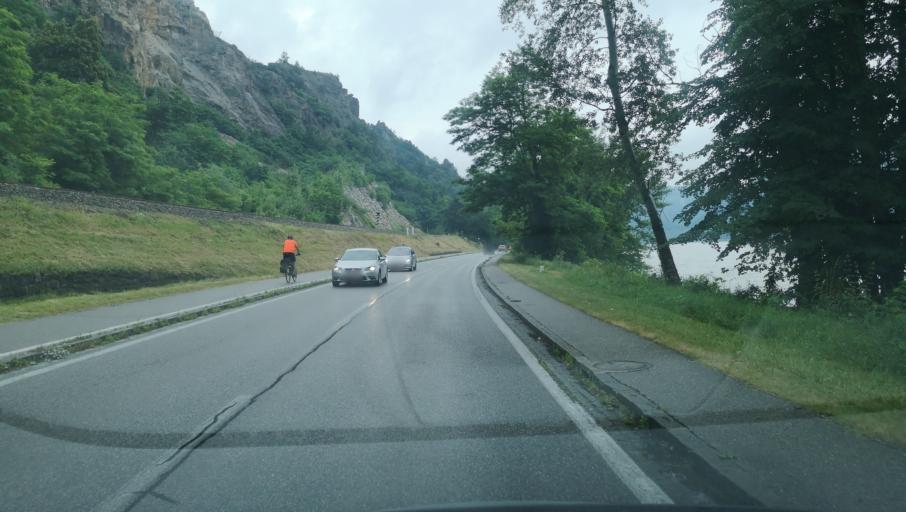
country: AT
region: Lower Austria
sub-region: Politischer Bezirk Krems
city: Durnstein
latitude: 48.4025
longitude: 15.5163
